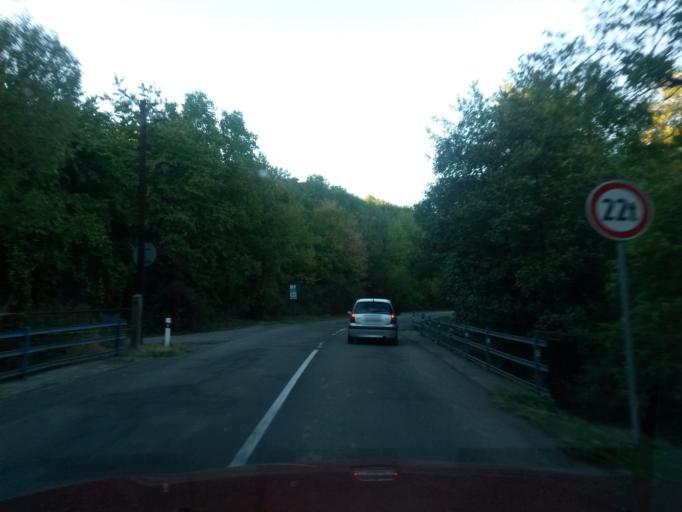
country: SK
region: Kosicky
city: Sobrance
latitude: 48.7844
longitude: 22.2482
